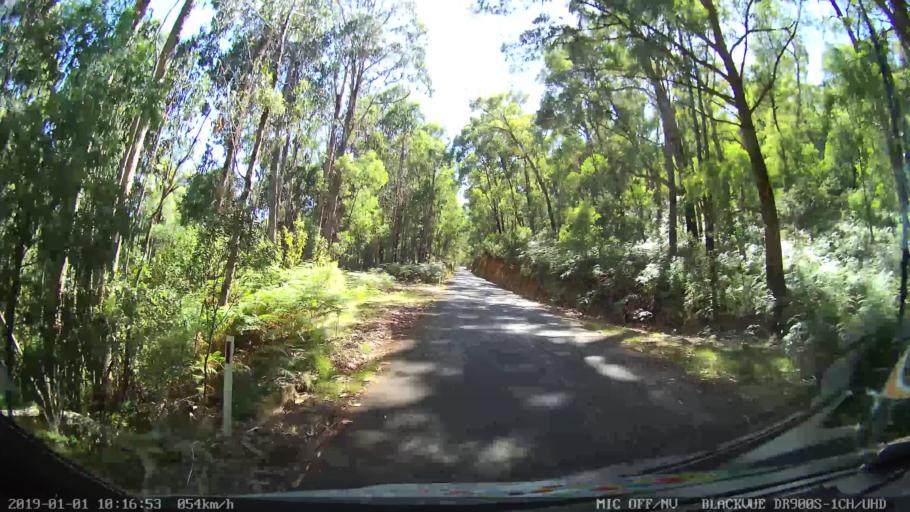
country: AU
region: New South Wales
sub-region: Snowy River
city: Jindabyne
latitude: -36.0927
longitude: 148.1715
